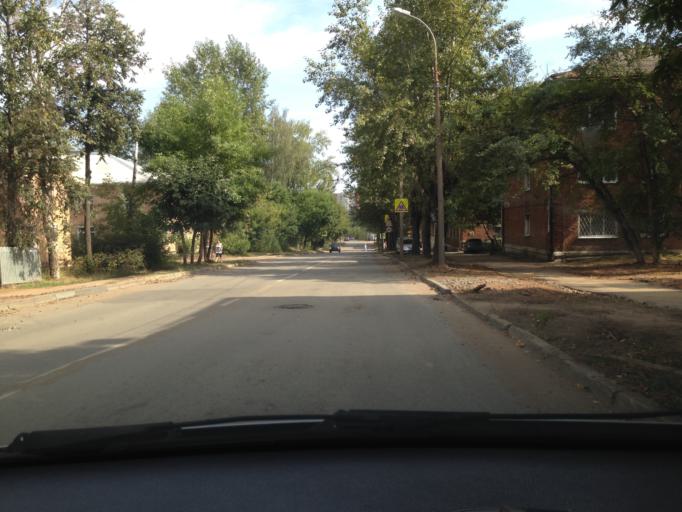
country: RU
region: Udmurtiya
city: Izhevsk
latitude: 56.8733
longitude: 53.1902
